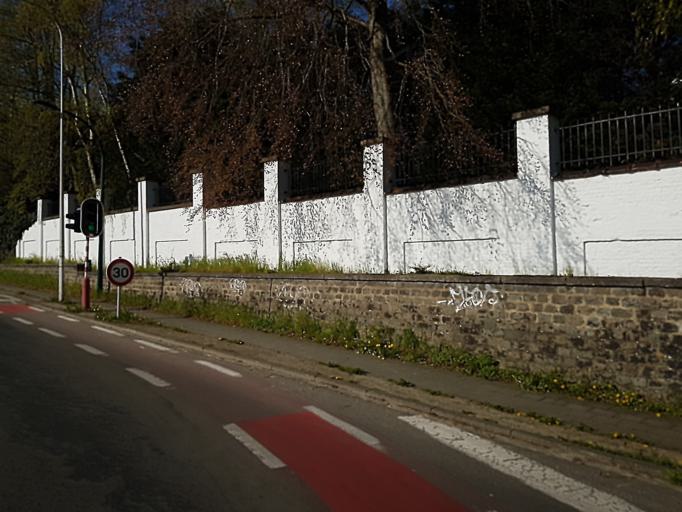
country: BE
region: Flanders
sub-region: Provincie Vlaams-Brabant
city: Sint-Genesius-Rode
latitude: 50.7475
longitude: 4.3631
